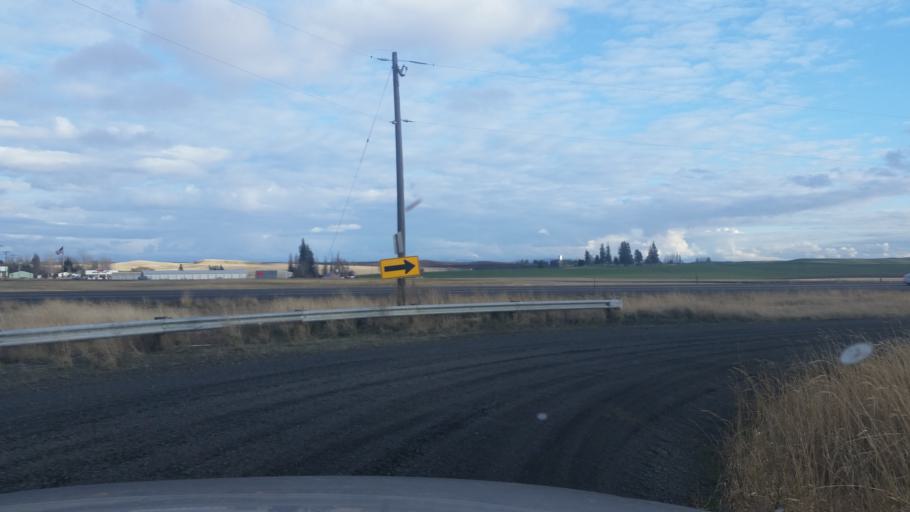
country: US
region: Washington
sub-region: Spokane County
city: Cheney
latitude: 47.4273
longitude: -117.3897
